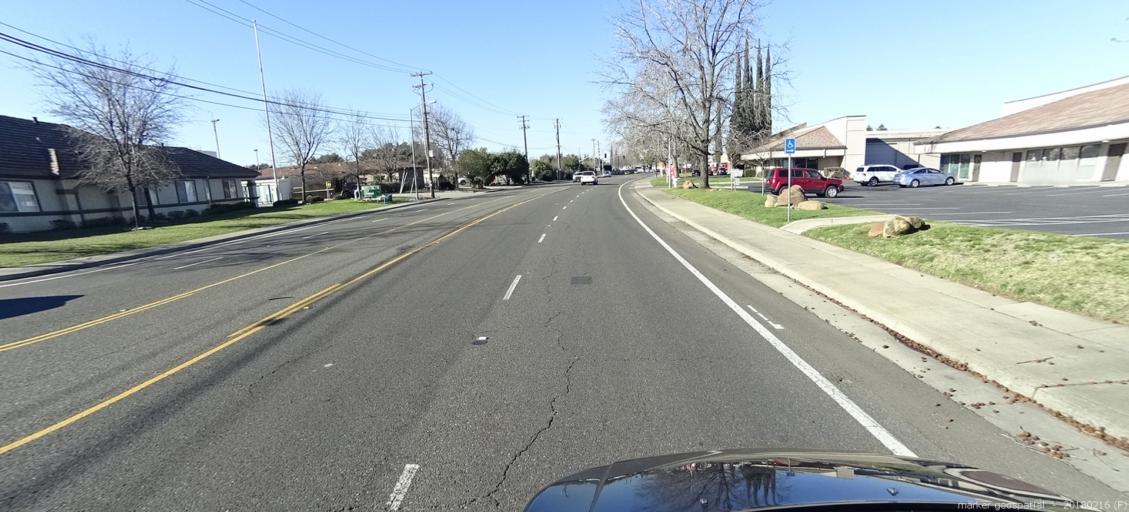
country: US
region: California
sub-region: Sacramento County
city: Gold River
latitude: 38.6191
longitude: -121.2640
